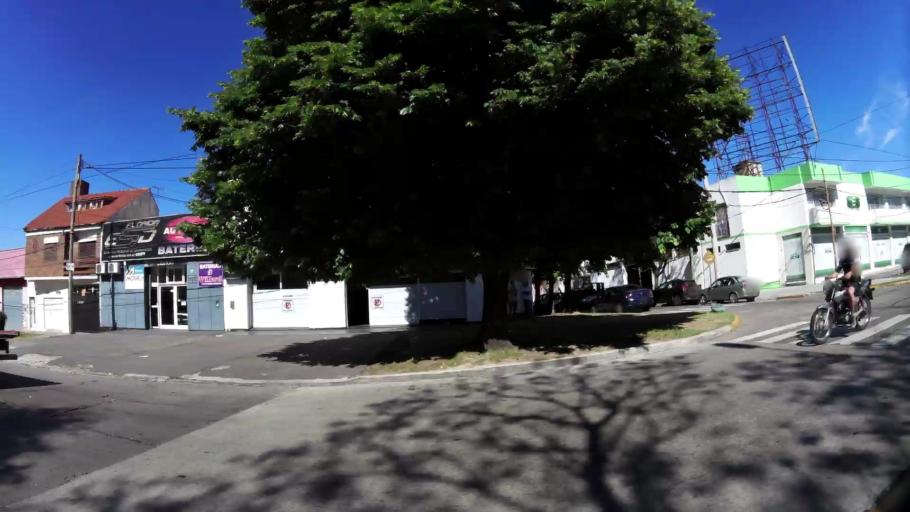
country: AR
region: Buenos Aires
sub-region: Partido de Vicente Lopez
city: Olivos
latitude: -34.5370
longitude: -58.5082
